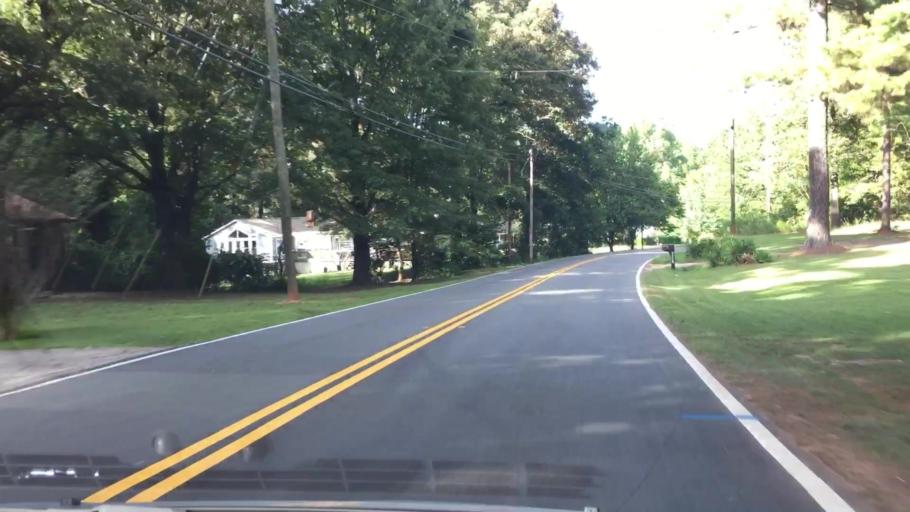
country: US
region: Georgia
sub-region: Henry County
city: Stockbridge
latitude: 33.5791
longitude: -84.1879
